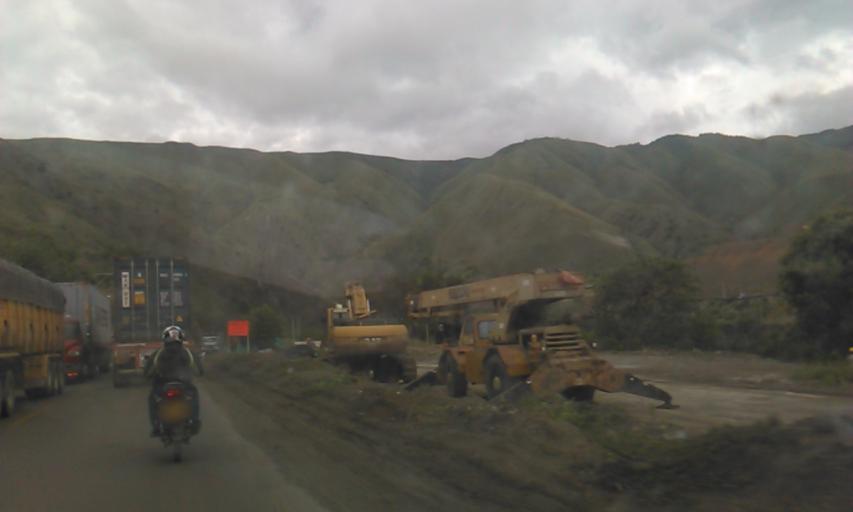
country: CO
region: Valle del Cauca
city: Dagua
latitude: 3.7603
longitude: -76.6618
